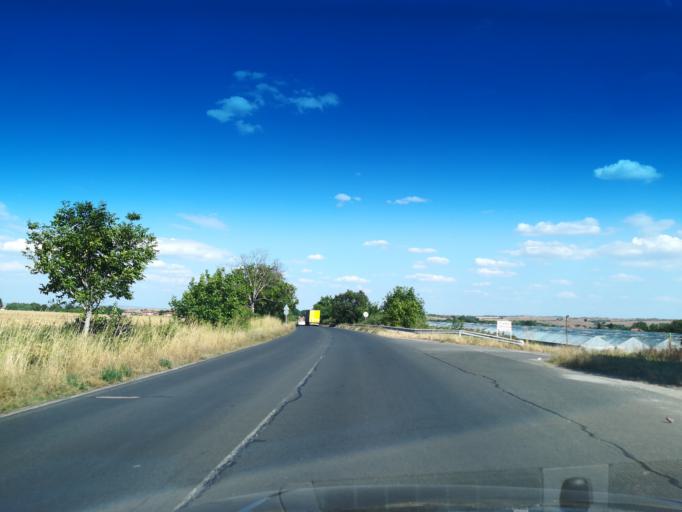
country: BG
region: Stara Zagora
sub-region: Obshtina Chirpan
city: Chirpan
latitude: 42.0585
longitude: 25.2508
